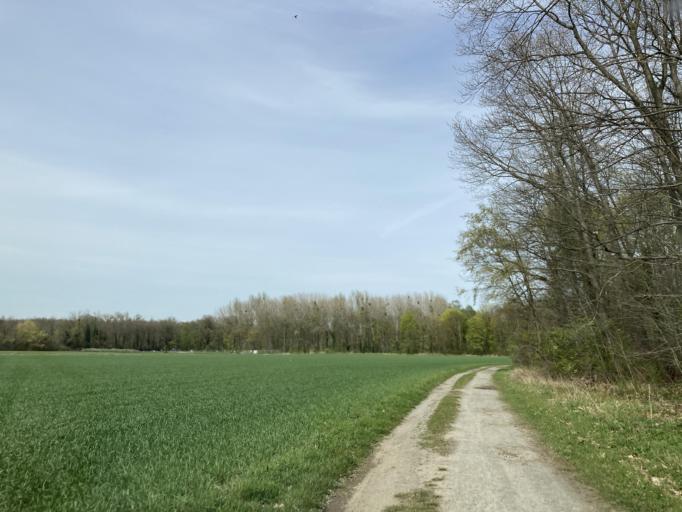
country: DE
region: Baden-Wuerttemberg
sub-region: Karlsruhe Region
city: Weingarten
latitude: 49.0742
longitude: 8.5338
